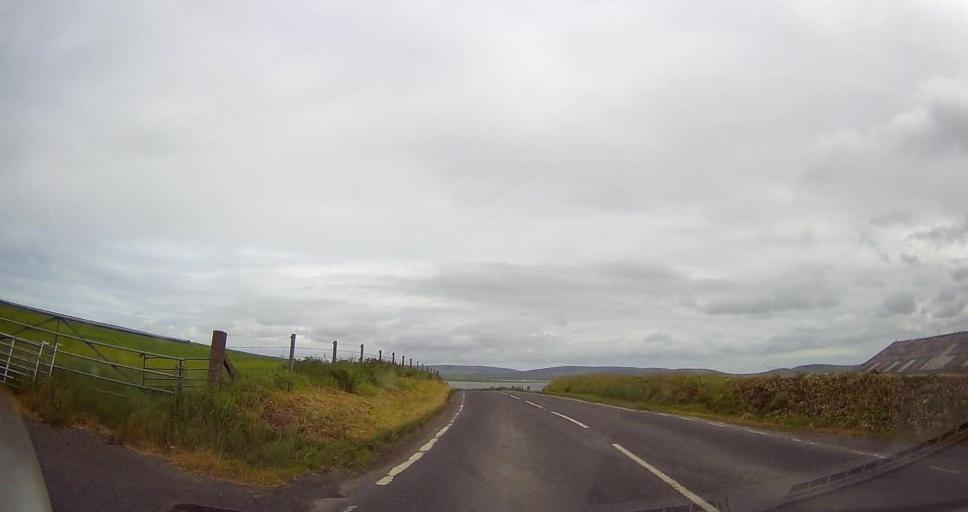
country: GB
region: Scotland
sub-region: Orkney Islands
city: Stromness
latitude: 58.9792
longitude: -3.2654
